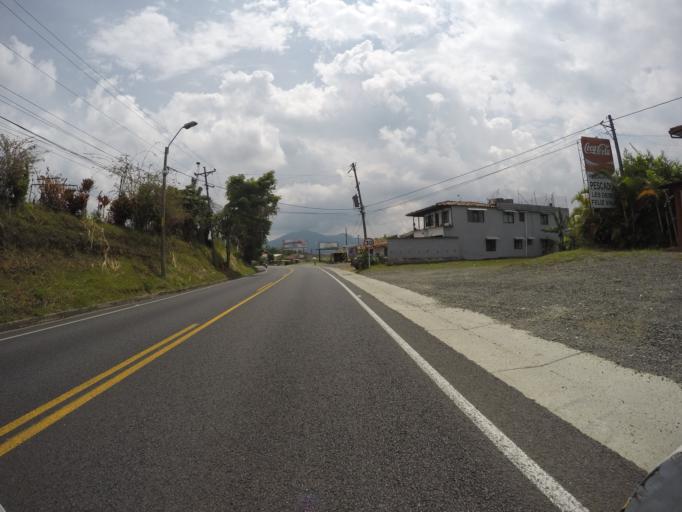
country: CO
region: Risaralda
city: Pereira
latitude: 4.7766
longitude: -75.6930
